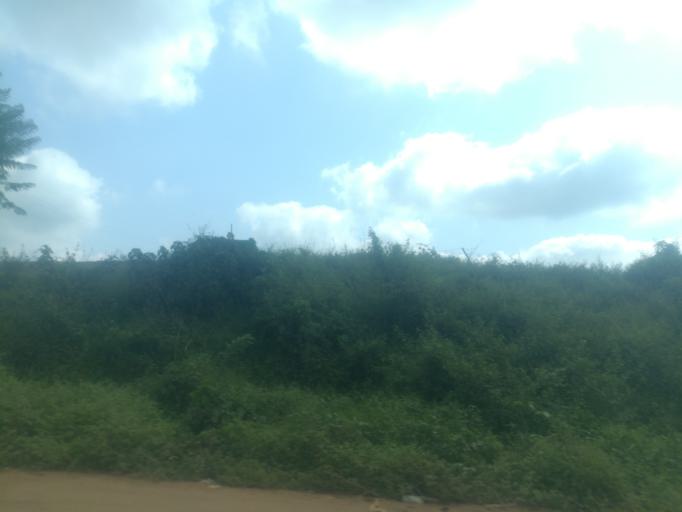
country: NG
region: Oyo
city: Moniya
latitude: 7.5714
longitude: 3.9147
